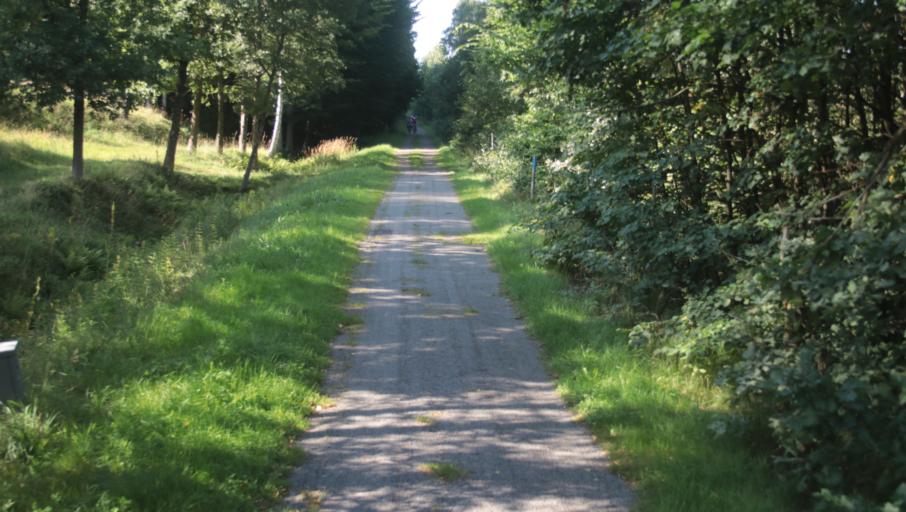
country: SE
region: Blekinge
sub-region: Karlshamns Kommun
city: Svangsta
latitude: 56.2759
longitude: 14.7590
